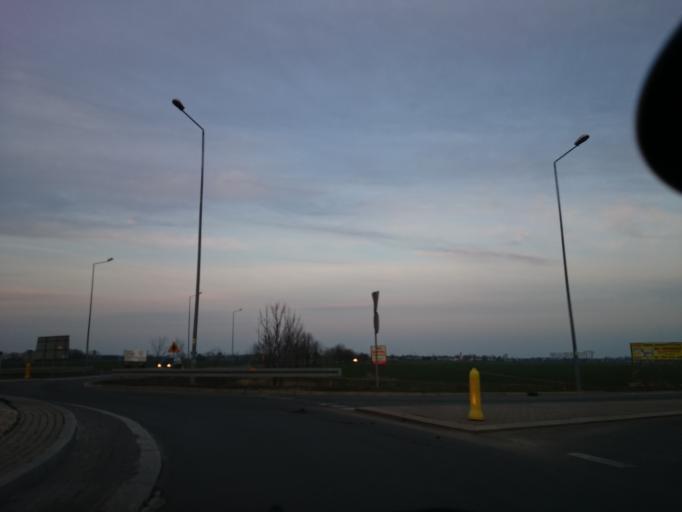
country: PL
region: Opole Voivodeship
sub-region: Powiat prudnicki
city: Lubrza
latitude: 50.3296
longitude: 17.6007
